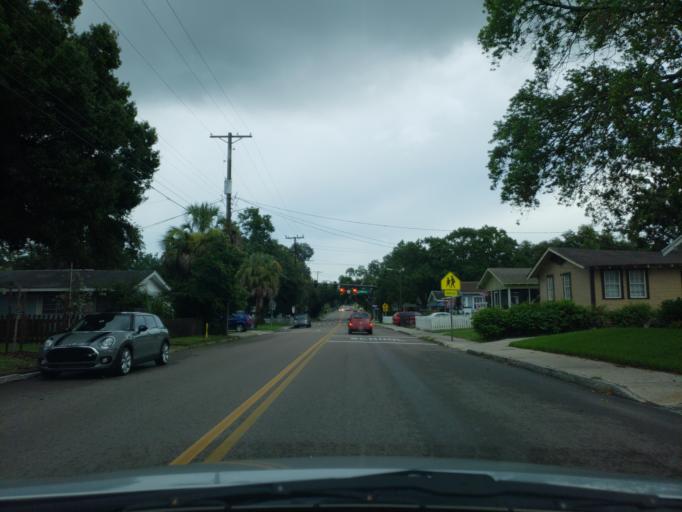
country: US
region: Florida
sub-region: Hillsborough County
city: Tampa
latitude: 27.9888
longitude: -82.4632
